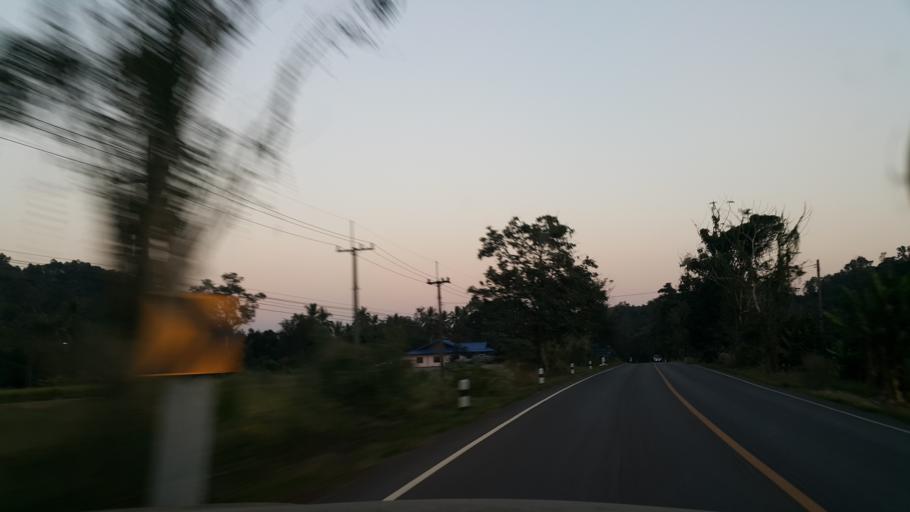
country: TH
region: Phrae
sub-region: Amphoe Wang Chin
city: Wang Chin
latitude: 17.9735
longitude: 99.6258
